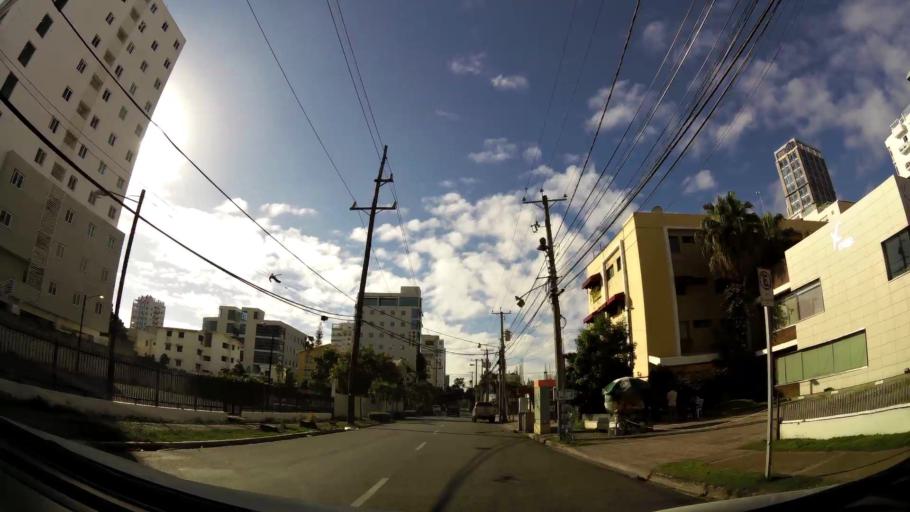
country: DO
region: Nacional
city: La Julia
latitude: 18.4716
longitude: -69.9387
